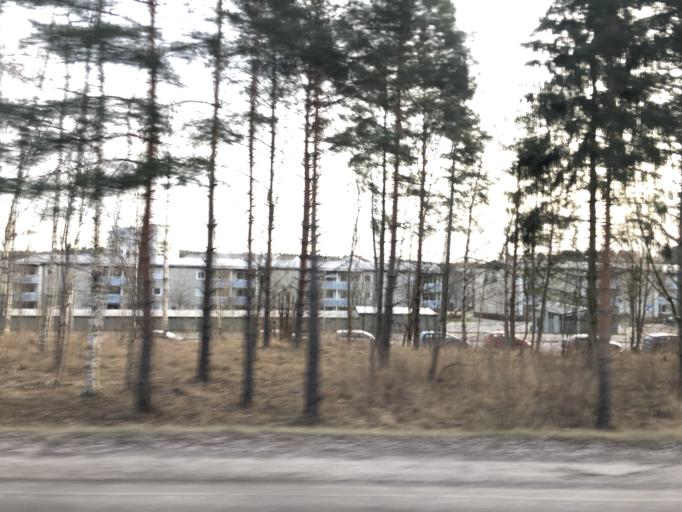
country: SE
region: Stockholm
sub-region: Jarfalla Kommun
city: Jakobsberg
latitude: 59.4115
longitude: 17.7966
